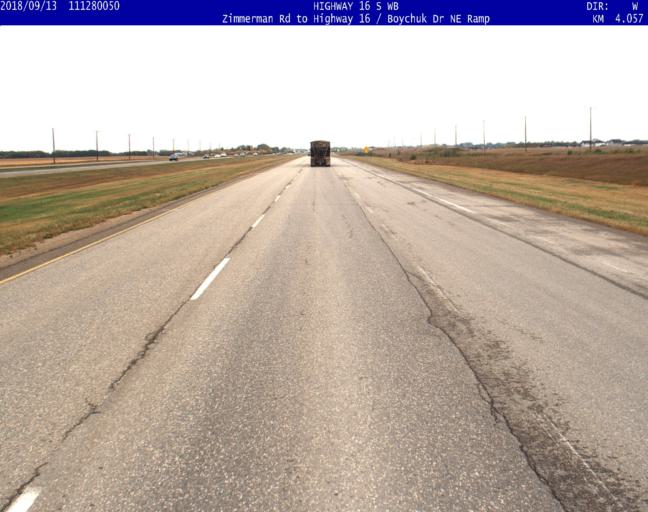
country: CA
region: Saskatchewan
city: Saskatoon
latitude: 52.0862
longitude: -106.5394
